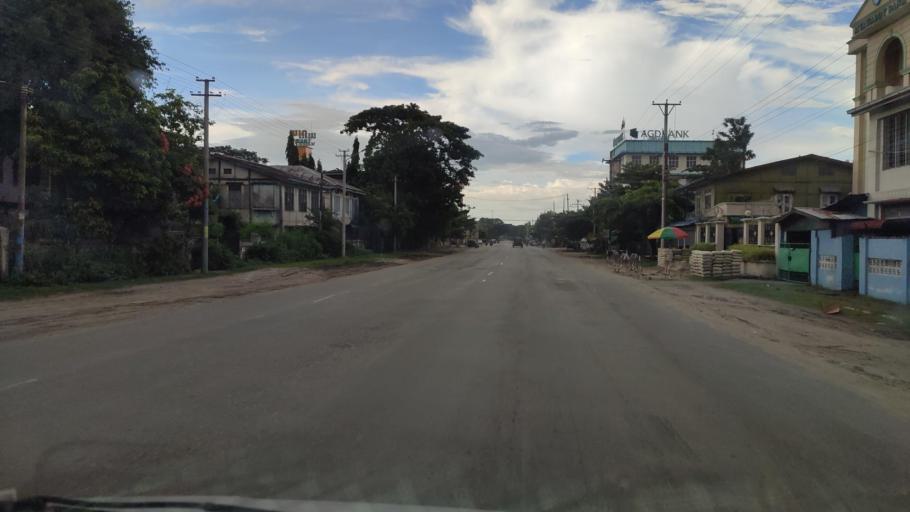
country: MM
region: Bago
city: Taungoo
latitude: 18.9462
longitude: 96.4429
